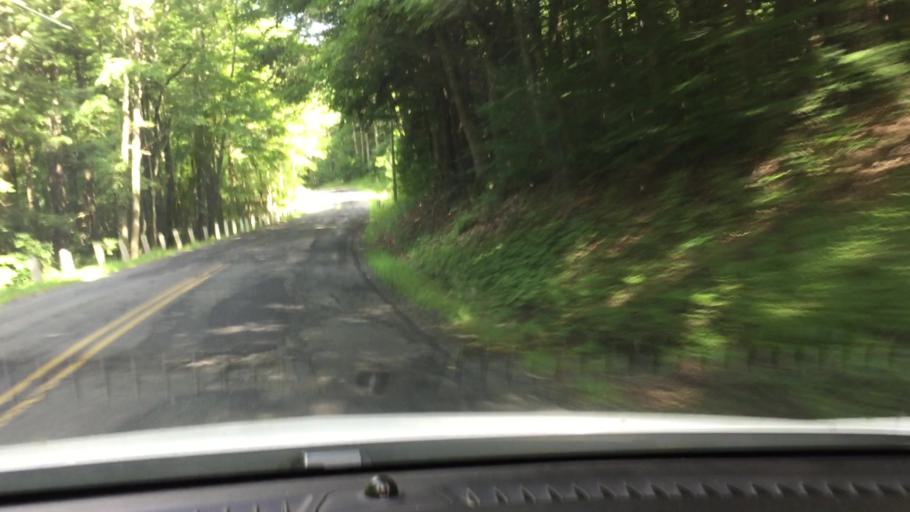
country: US
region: Massachusetts
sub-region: Berkshire County
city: Otis
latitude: 42.1930
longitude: -73.1580
